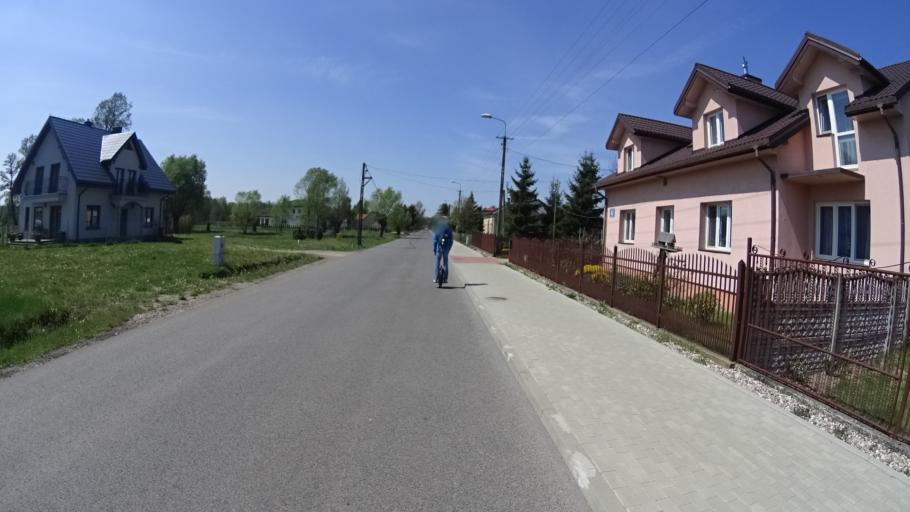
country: PL
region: Masovian Voivodeship
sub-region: Powiat warszawski zachodni
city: Truskaw
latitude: 52.2831
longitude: 20.7370
